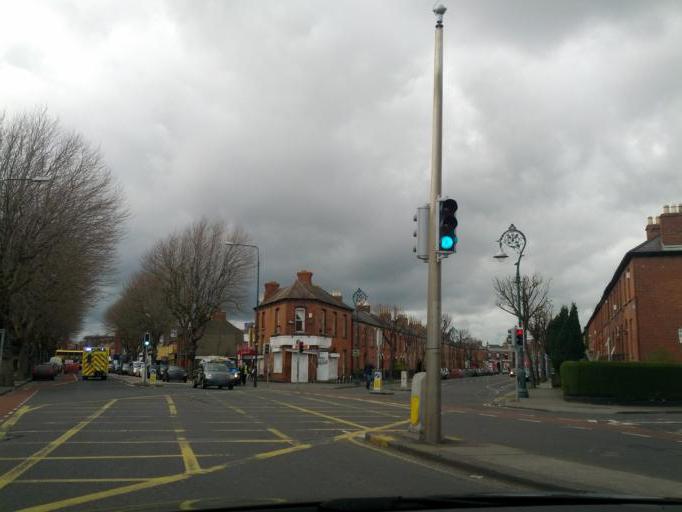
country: IE
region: Leinster
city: Drumcondra
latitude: 53.3591
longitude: -6.2585
